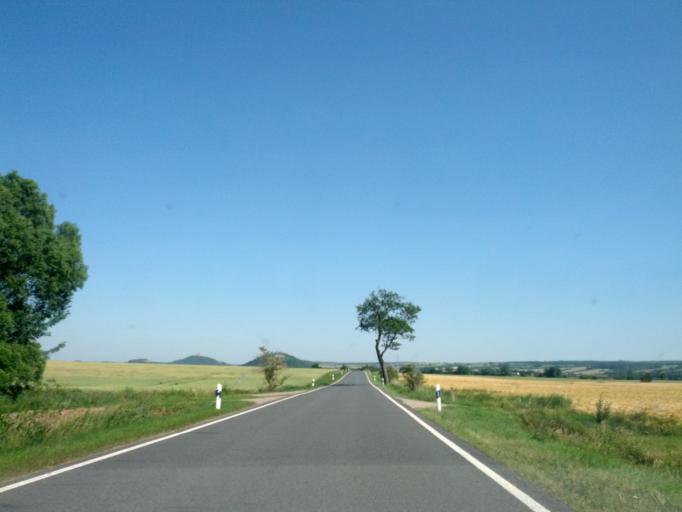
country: DE
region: Thuringia
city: Seebergen
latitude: 50.8857
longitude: 10.7931
